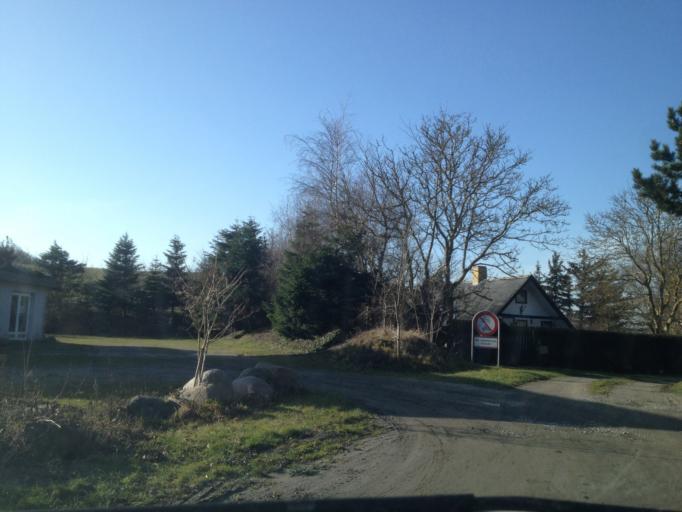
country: DK
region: South Denmark
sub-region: Kerteminde Kommune
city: Munkebo
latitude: 55.5746
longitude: 10.6034
